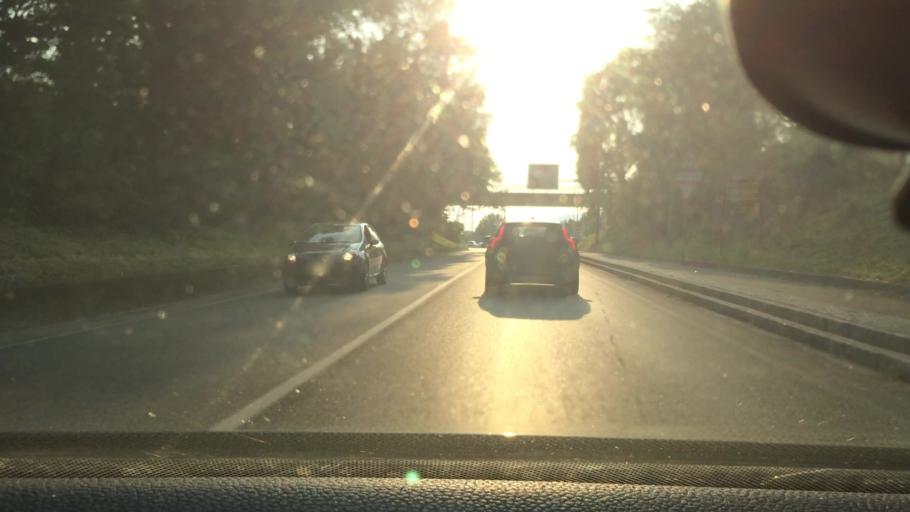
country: IT
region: Lombardy
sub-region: Provincia di Bergamo
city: Curno
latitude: 45.6902
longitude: 9.6330
